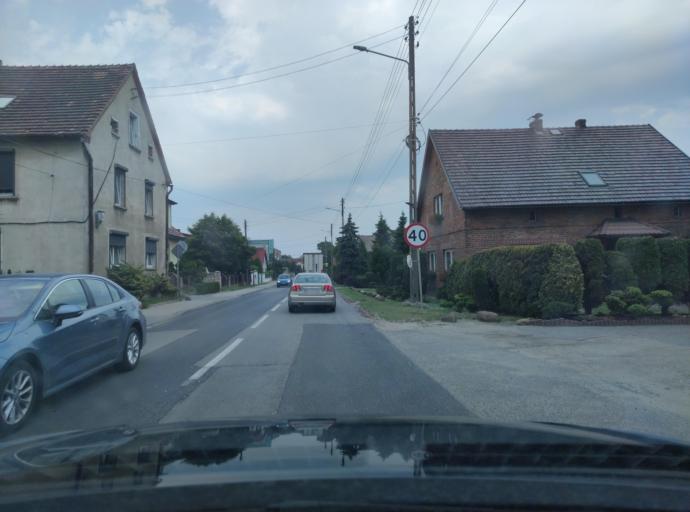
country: PL
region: Opole Voivodeship
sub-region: Powiat strzelecki
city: Strzelce Opolskie
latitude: 50.5010
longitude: 18.2917
